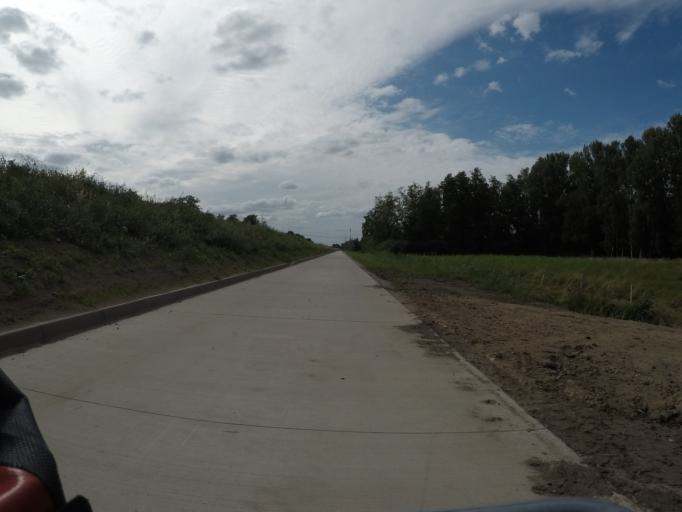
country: DE
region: Lower Saxony
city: Handorf
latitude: 53.3562
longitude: 10.3534
